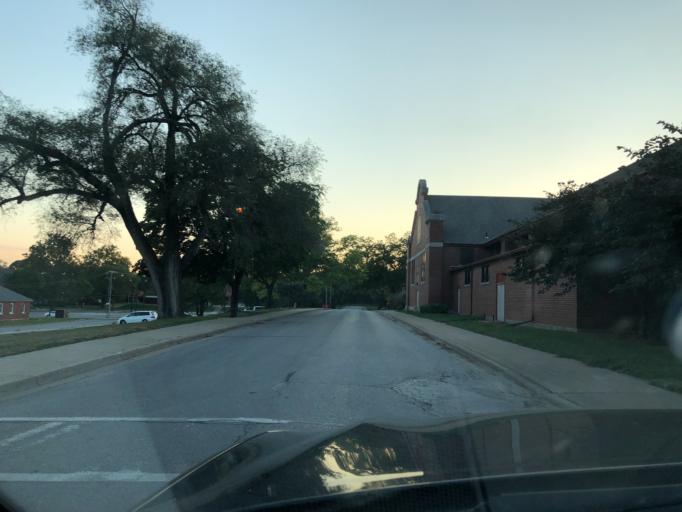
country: US
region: Kansas
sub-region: Leavenworth County
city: Leavenworth
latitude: 39.3488
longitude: -94.9152
